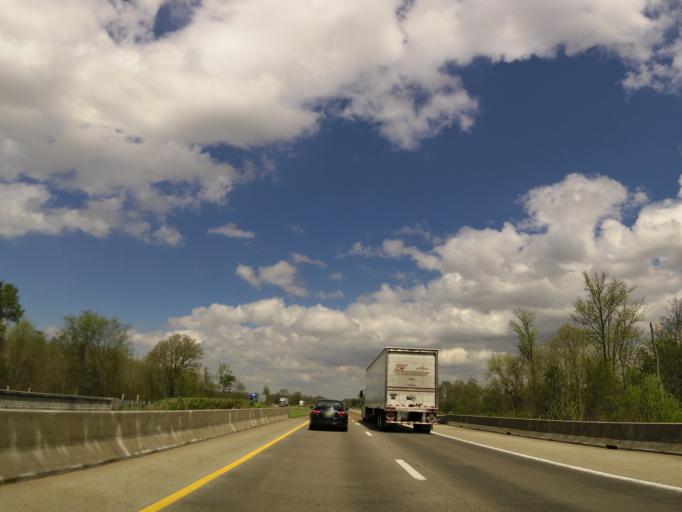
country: US
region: Tennessee
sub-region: Fayette County
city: Hickory Withe
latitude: 35.3104
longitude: -89.5845
